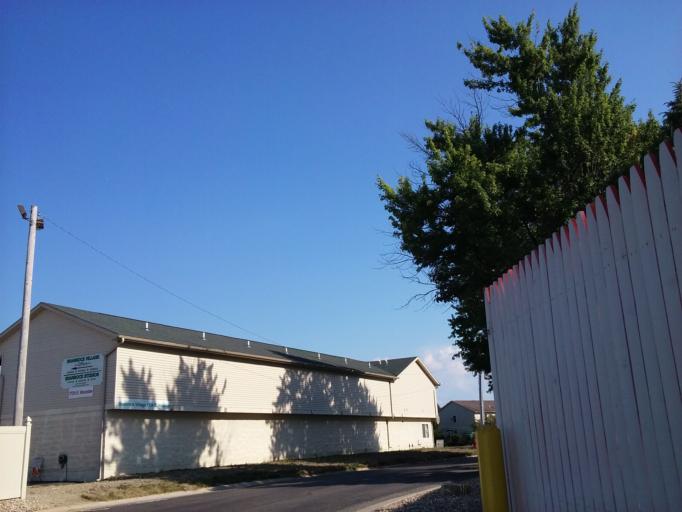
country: US
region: Ohio
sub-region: Wood County
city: Bowling Green
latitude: 41.3730
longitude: -83.6194
